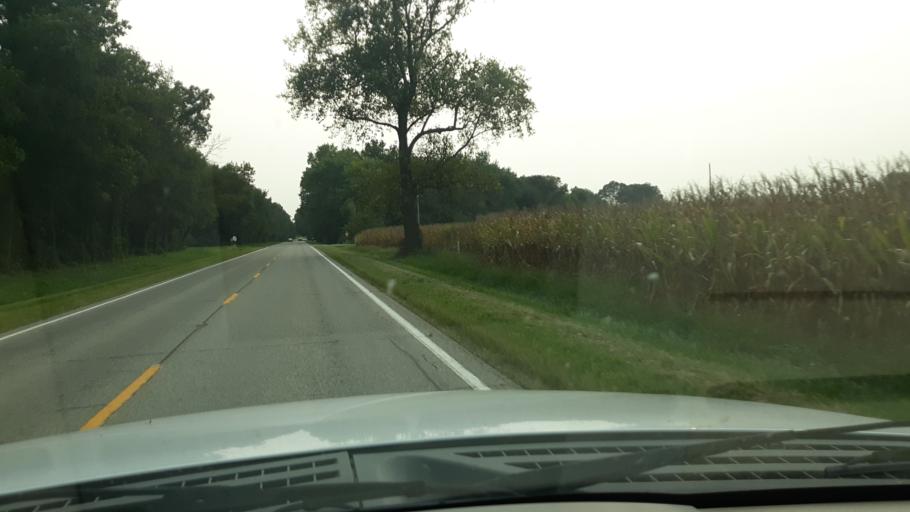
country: US
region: Illinois
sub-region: Edwards County
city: Grayville
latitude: 38.3183
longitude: -87.9254
